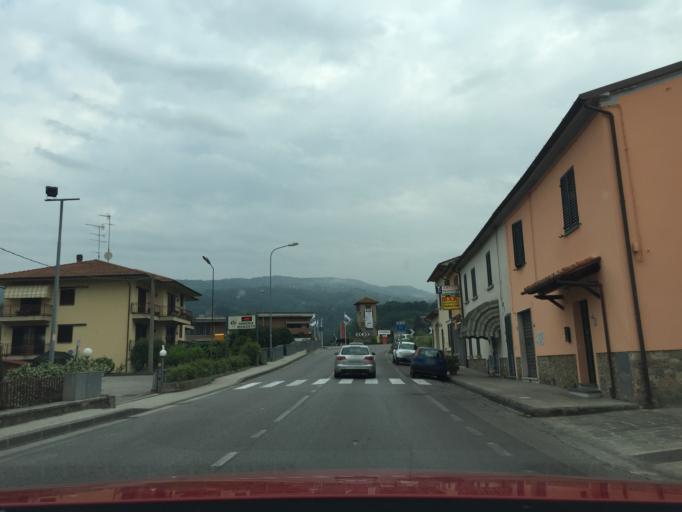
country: IT
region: Tuscany
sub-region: Provincia di Pistoia
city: Serravalle Pistoiese
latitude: 43.8973
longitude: 10.8224
